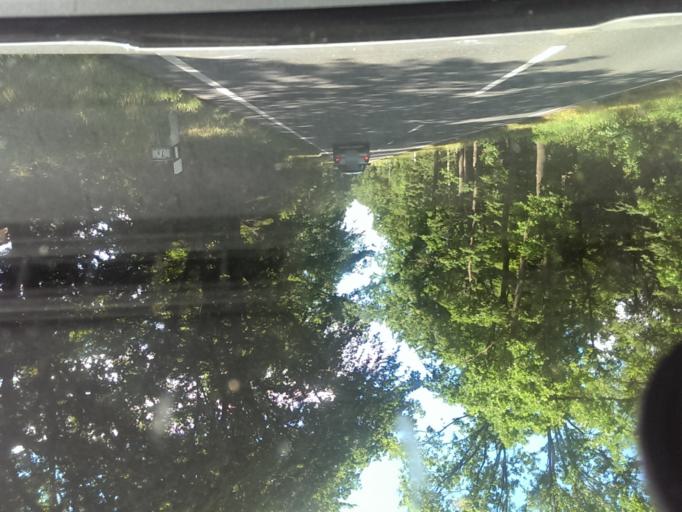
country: DE
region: Lower Saxony
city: Ahausen
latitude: 53.0139
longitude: 9.2757
